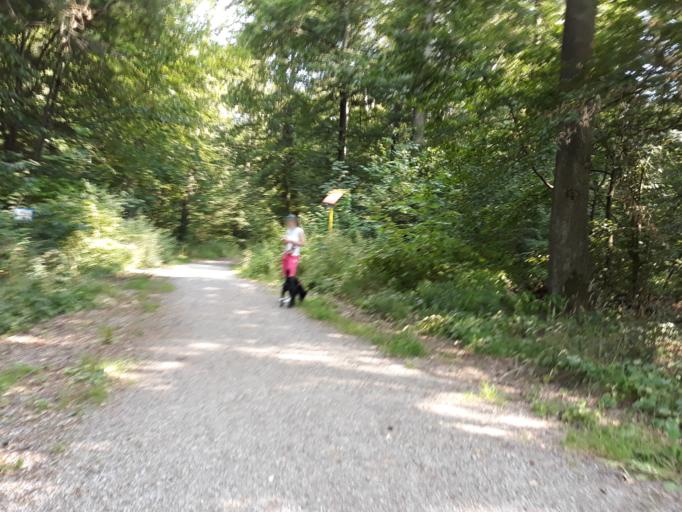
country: DE
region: Baden-Wuerttemberg
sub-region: Regierungsbezirk Stuttgart
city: Boeblingen
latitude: 48.6788
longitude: 9.0388
